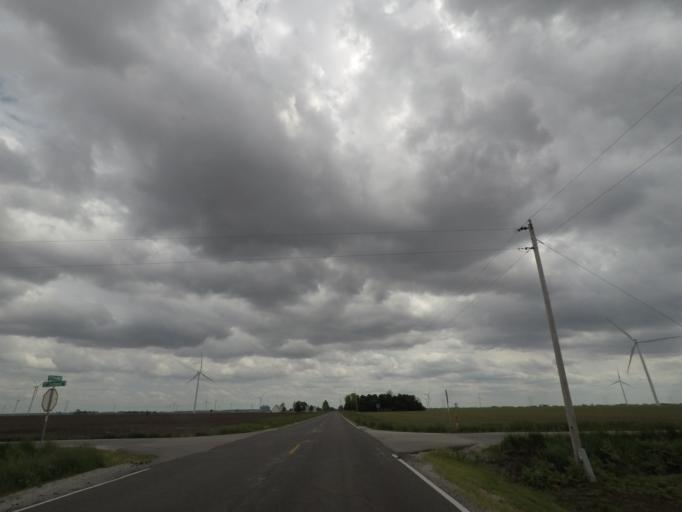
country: US
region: Illinois
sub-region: Macon County
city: Warrensburg
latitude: 40.0060
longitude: -89.0856
